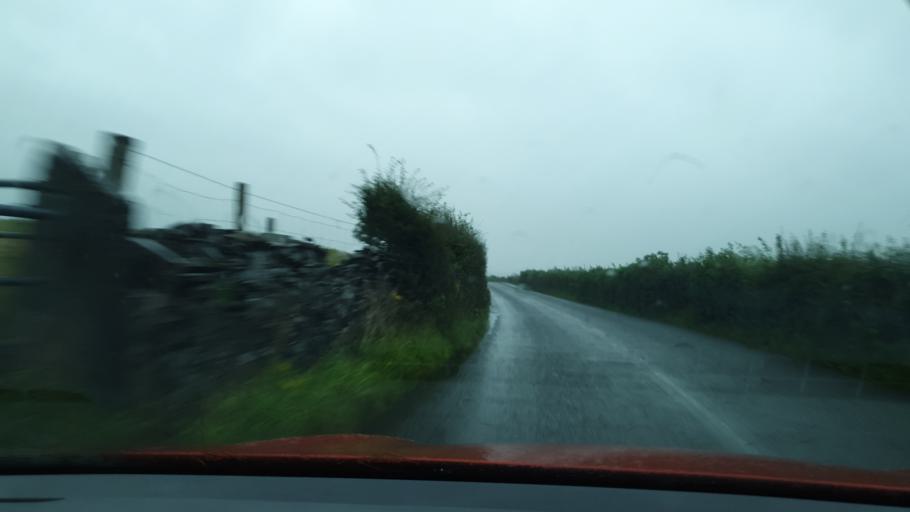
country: GB
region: England
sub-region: Cumbria
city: Millom
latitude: 54.2751
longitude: -3.2216
